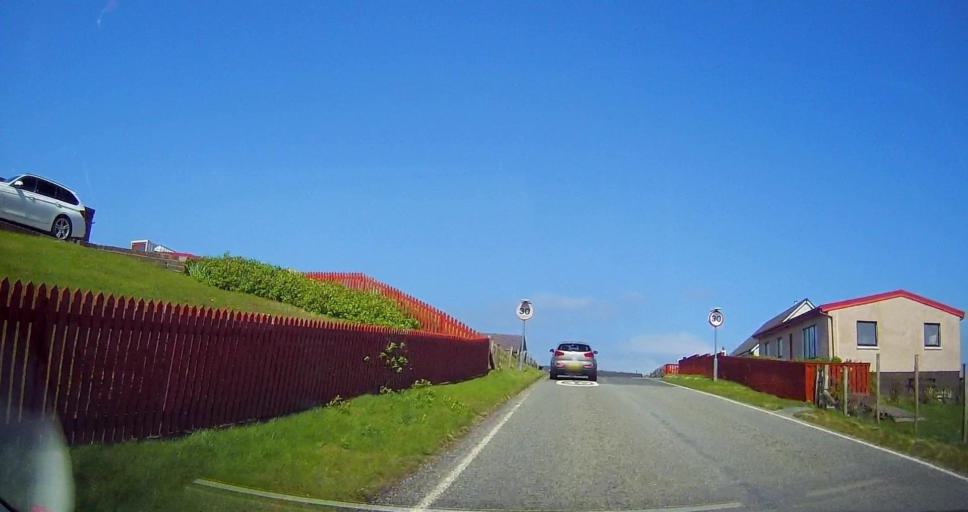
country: GB
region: Scotland
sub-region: Shetland Islands
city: Sandwick
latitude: 60.0955
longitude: -1.3216
